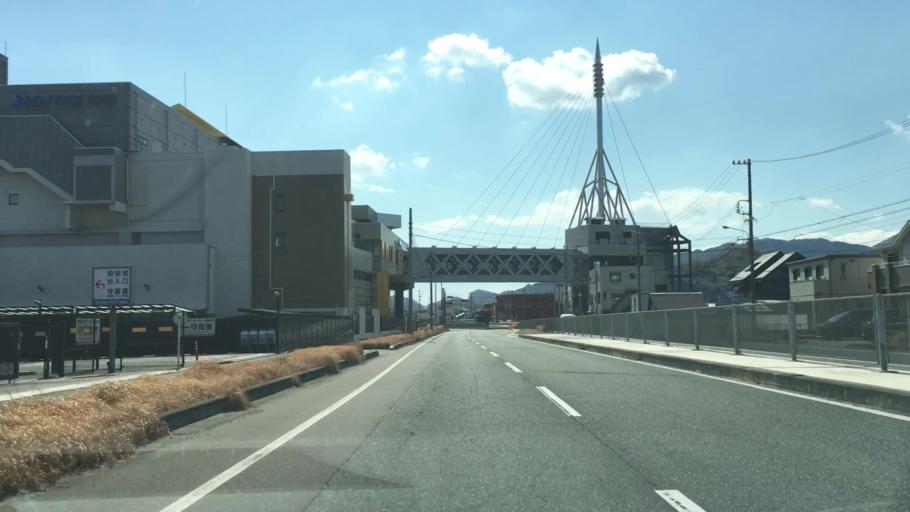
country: JP
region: Aichi
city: Gamagori
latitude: 34.8244
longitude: 137.2058
